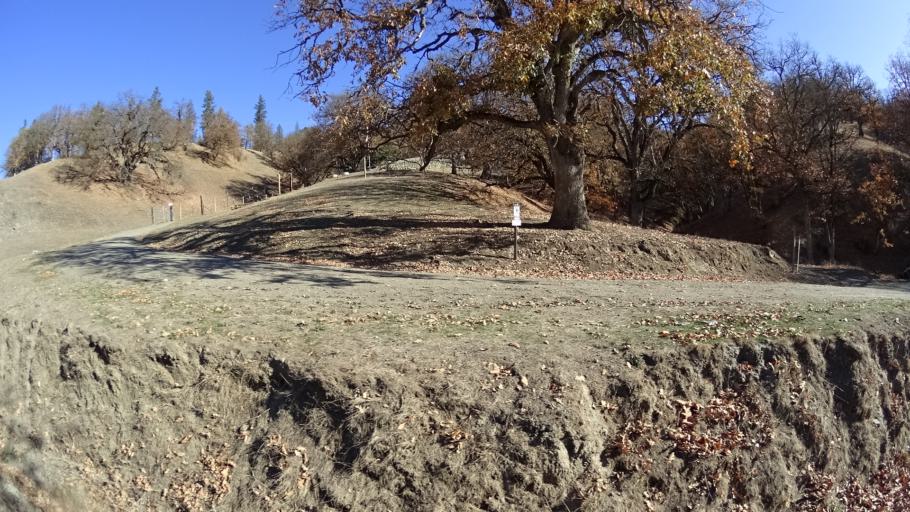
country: US
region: California
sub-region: Siskiyou County
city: Happy Camp
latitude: 41.8329
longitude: -123.0050
